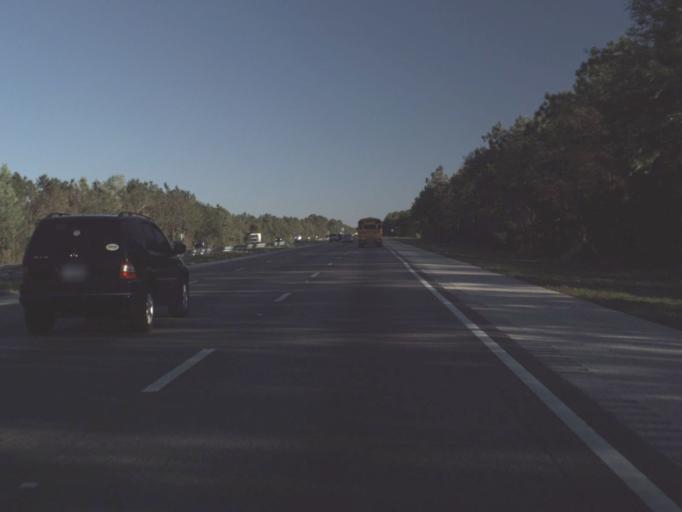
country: US
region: Florida
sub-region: Flagler County
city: Flagler Beach
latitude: 29.4578
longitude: -81.1770
